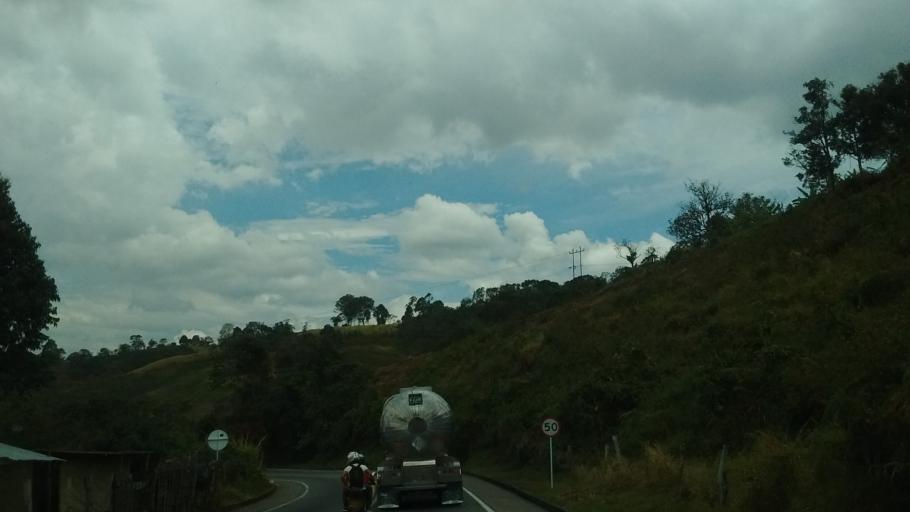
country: CO
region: Cauca
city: Rosas
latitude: 2.3082
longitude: -76.6869
